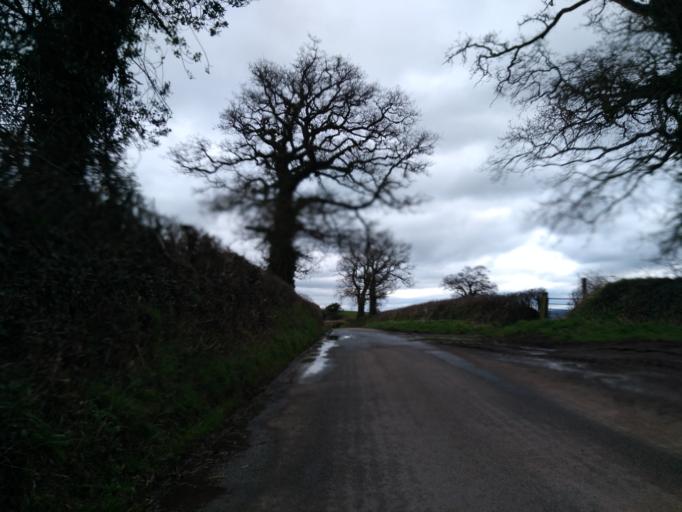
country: GB
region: England
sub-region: Devon
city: Crediton
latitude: 50.7869
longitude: -3.6149
